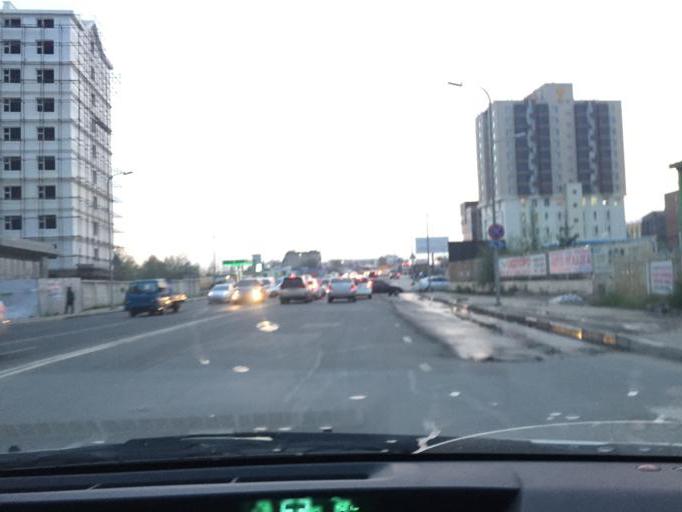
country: MN
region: Ulaanbaatar
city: Ulaanbaatar
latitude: 47.9236
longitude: 106.9507
